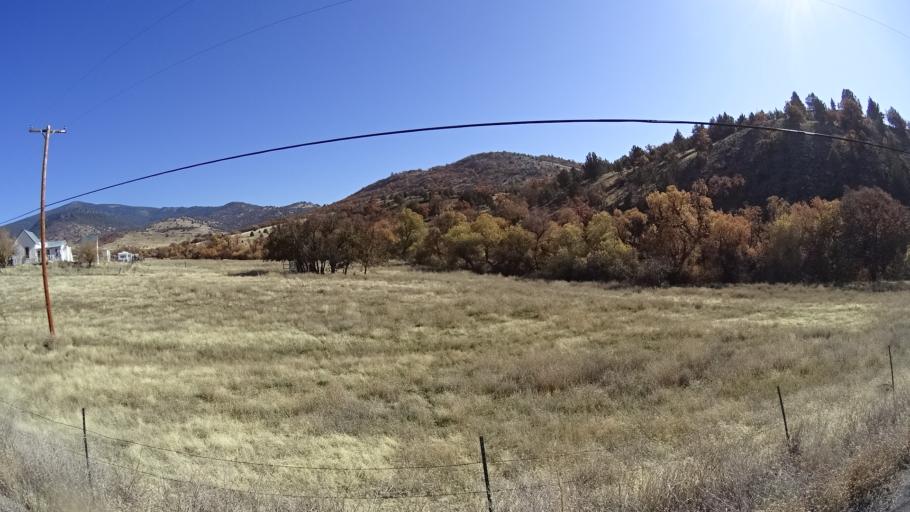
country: US
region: California
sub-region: Siskiyou County
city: Montague
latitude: 41.7936
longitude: -122.3424
